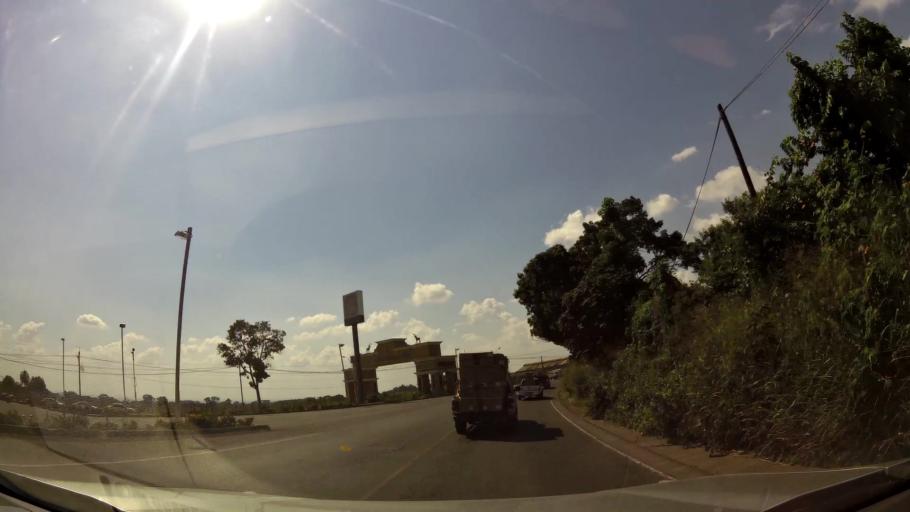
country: GT
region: Suchitepeque
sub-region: Municipio de San Gabriel
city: San Gabriel
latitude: 14.5356
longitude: -91.5240
